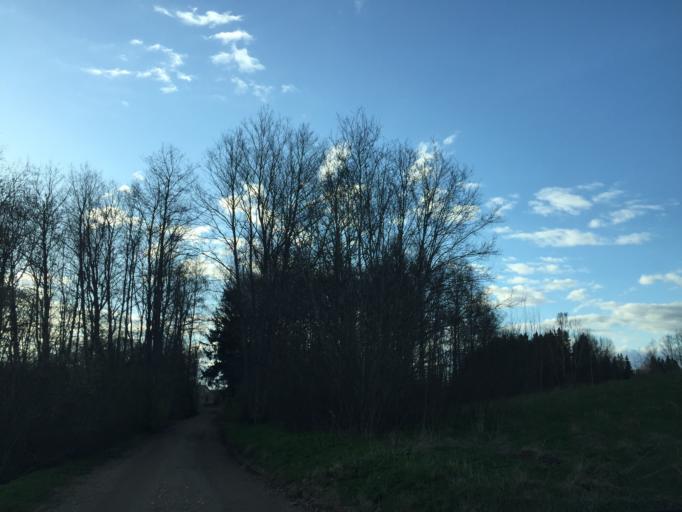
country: LV
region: Rezekne
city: Rezekne
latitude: 56.5825
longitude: 27.3565
